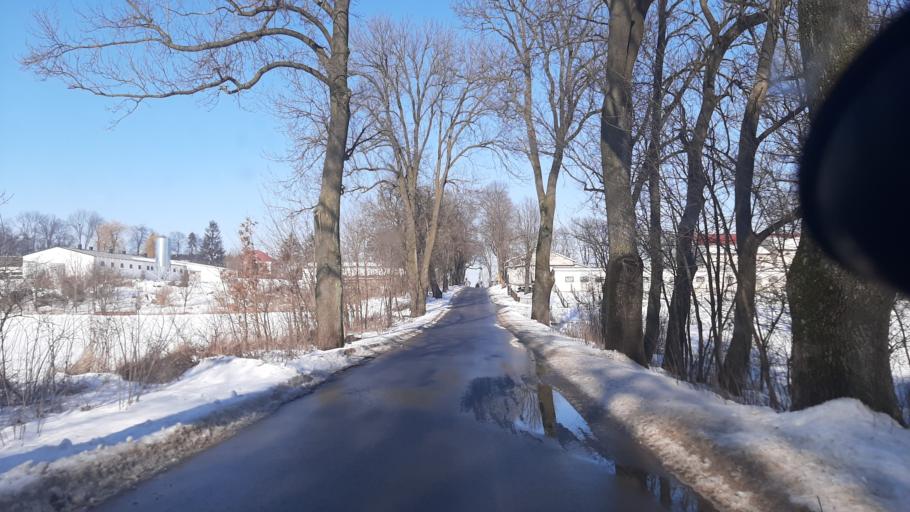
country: PL
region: Lublin Voivodeship
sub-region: Powiat pulawski
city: Naleczow
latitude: 51.3028
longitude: 22.2594
